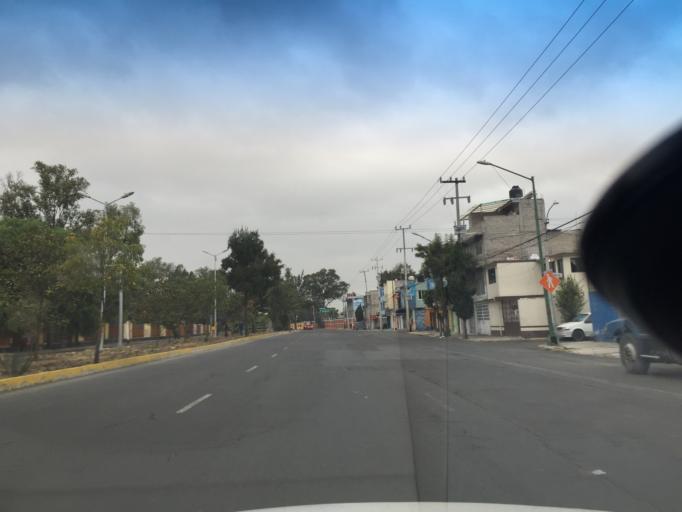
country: MX
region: Mexico City
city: Venustiano Carranza
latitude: 19.4667
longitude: -99.0740
